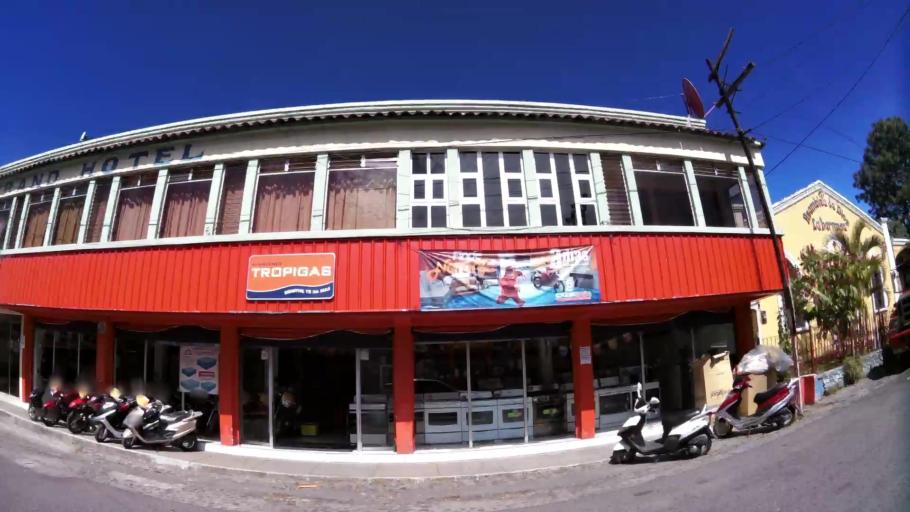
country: GT
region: Solola
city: Panajachel
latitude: 14.7441
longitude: -91.1570
